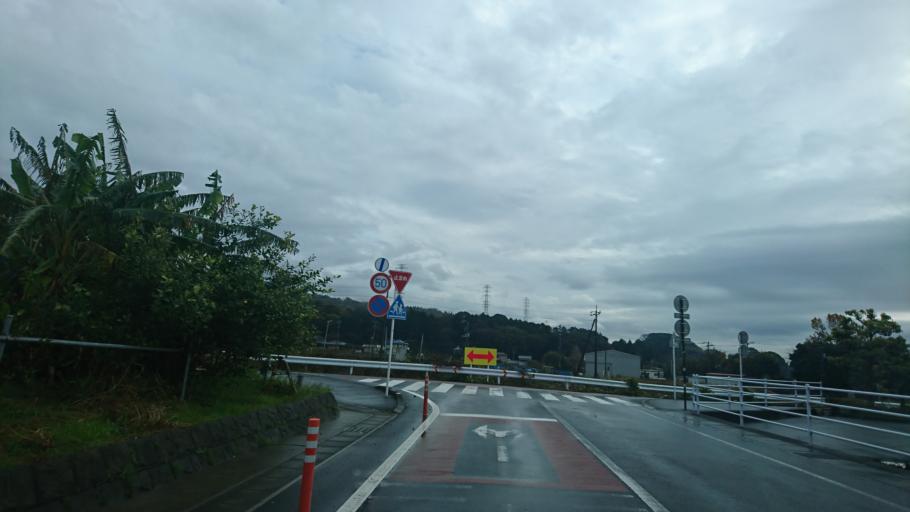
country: JP
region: Shizuoka
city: Fuji
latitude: 35.1676
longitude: 138.7391
